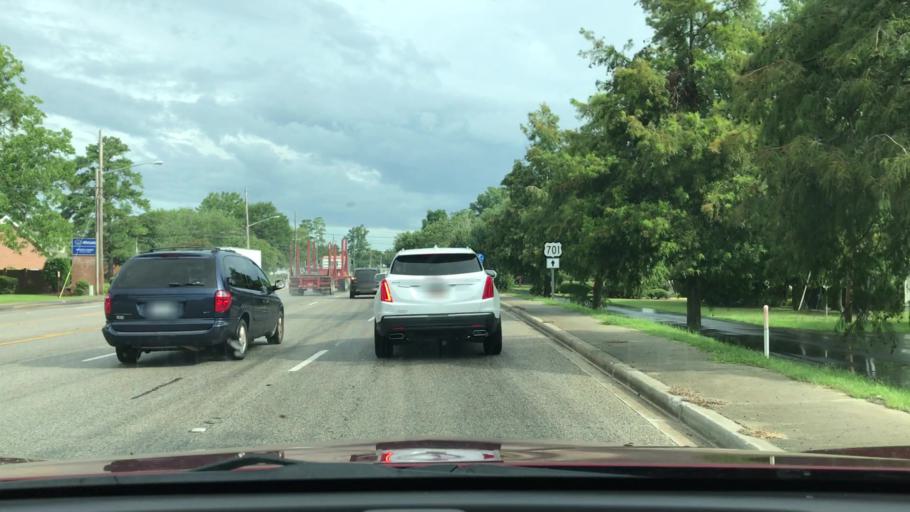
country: US
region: South Carolina
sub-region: Georgetown County
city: Georgetown
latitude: 33.3841
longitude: -79.2875
